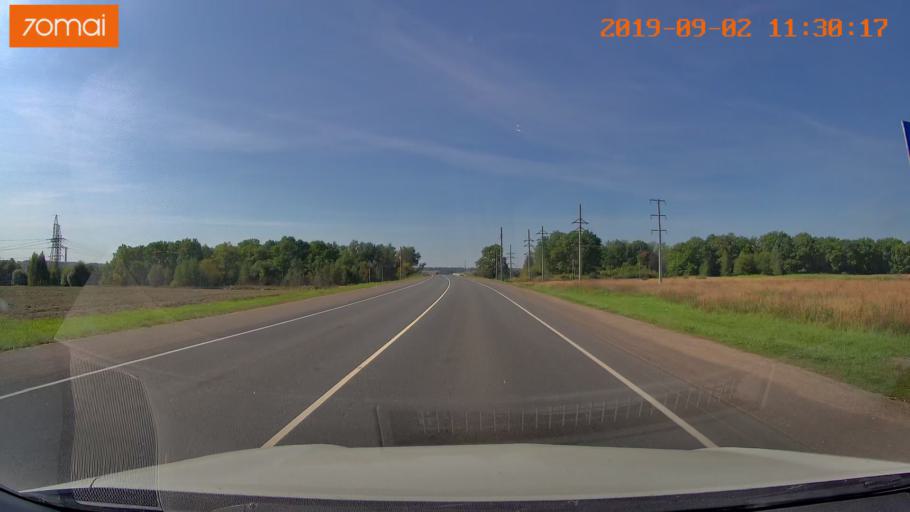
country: RU
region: Smolensk
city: Roslavl'
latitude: 53.9857
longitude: 32.8376
